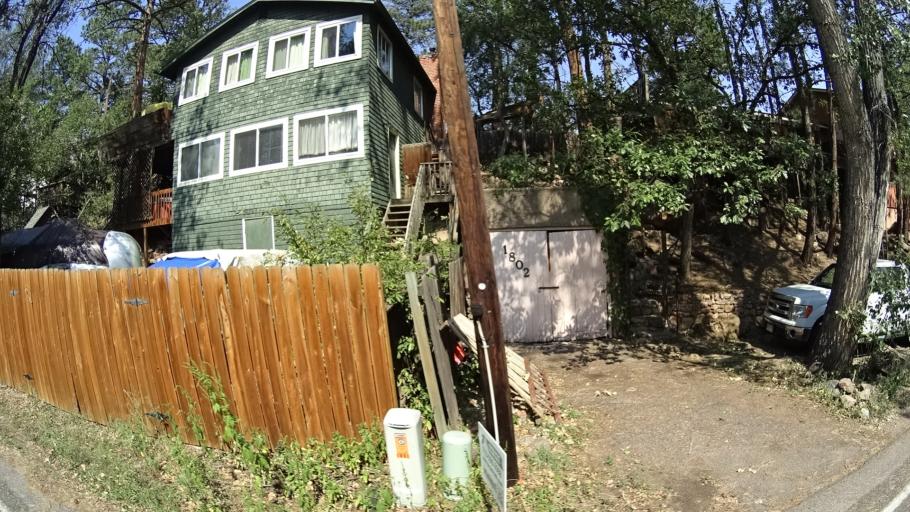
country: US
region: Colorado
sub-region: El Paso County
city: Colorado Springs
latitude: 38.7917
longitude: -104.8589
